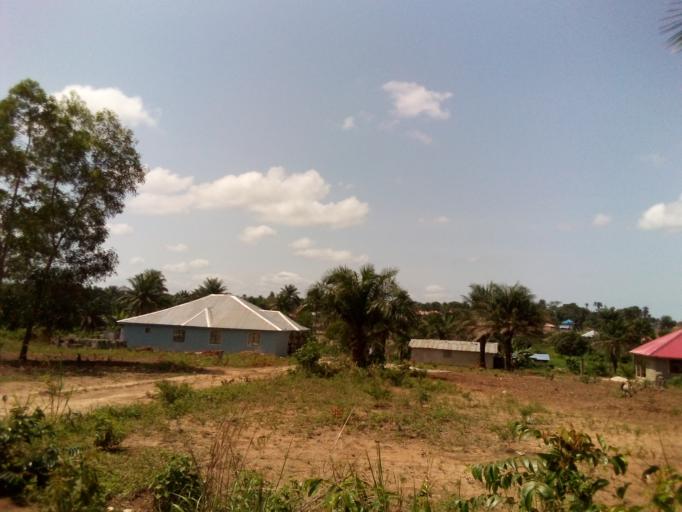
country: SL
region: Western Area
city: Waterloo
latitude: 8.3430
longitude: -13.0190
